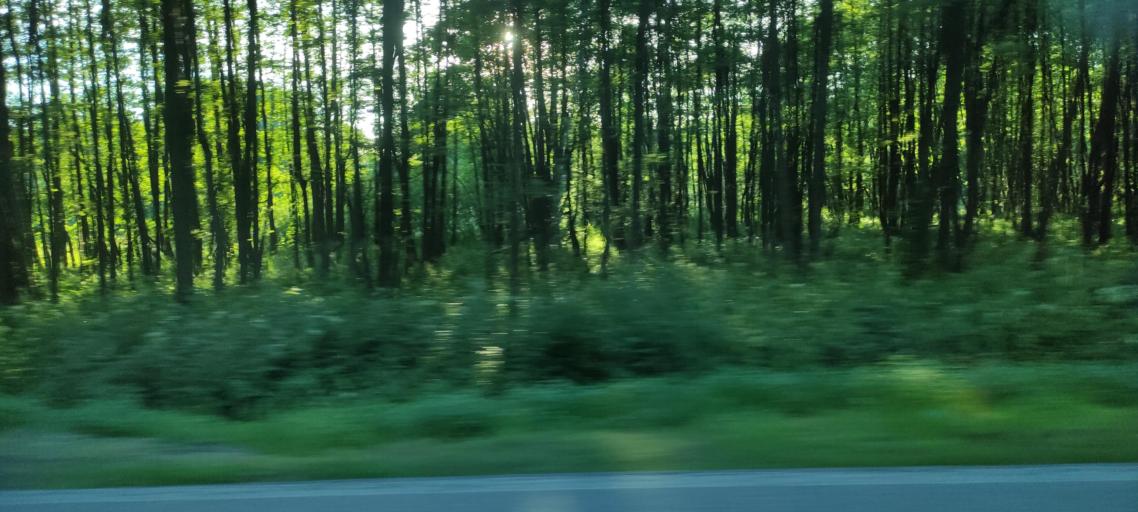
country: CZ
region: Jihocesky
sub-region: Okres Jindrichuv Hradec
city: Jindrichuv Hradec
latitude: 49.1150
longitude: 15.0019
